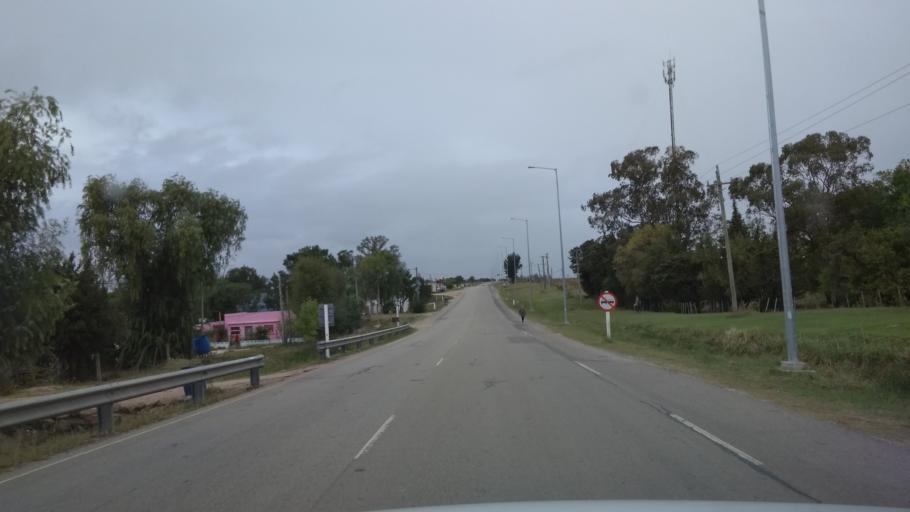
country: UY
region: Canelones
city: Tala
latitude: -34.2010
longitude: -55.7442
